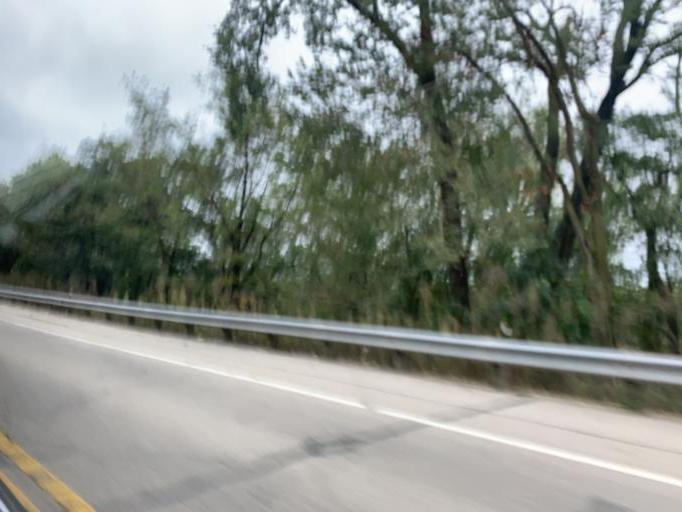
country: US
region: Wisconsin
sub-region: Grant County
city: Muscoda
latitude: 43.2056
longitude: -90.5762
